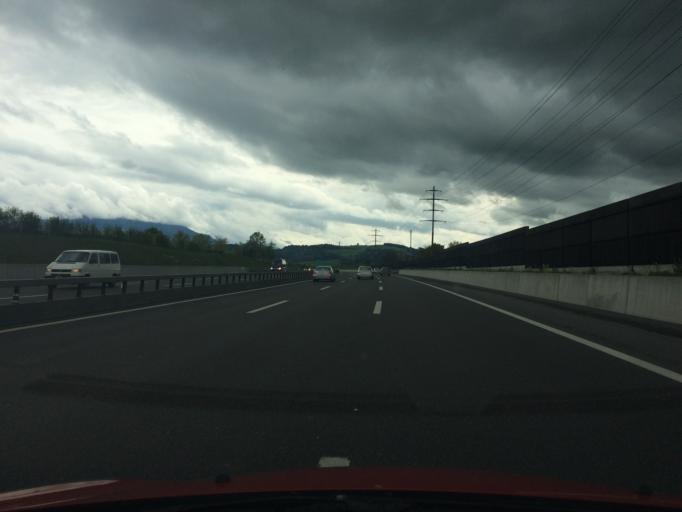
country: CH
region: Zug
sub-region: Zug
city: Hunenberg
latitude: 47.1765
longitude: 8.4326
